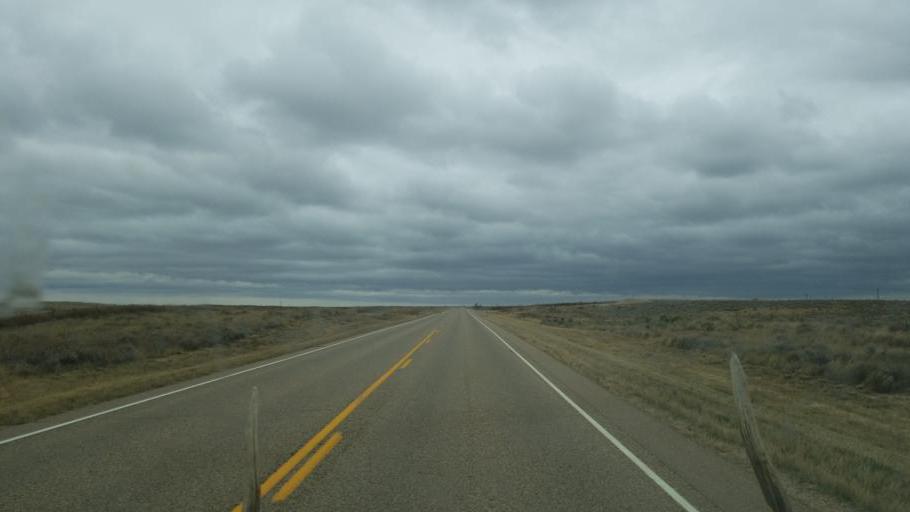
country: US
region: Colorado
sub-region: Cheyenne County
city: Cheyenne Wells
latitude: 38.7913
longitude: -102.6694
